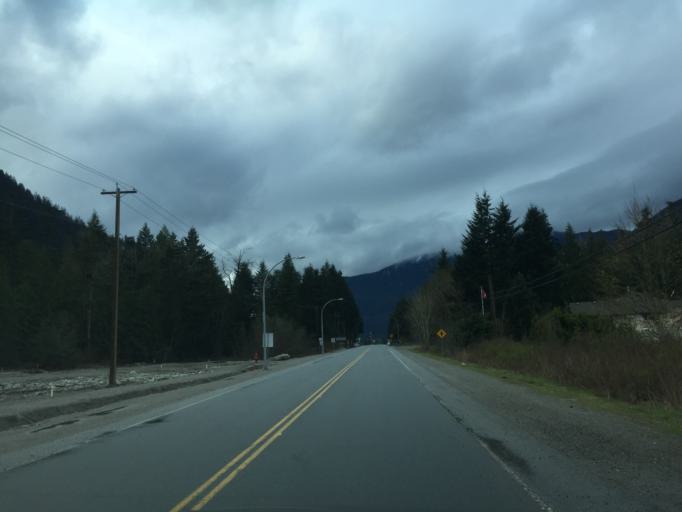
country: CA
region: British Columbia
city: Hope
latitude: 49.3617
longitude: -121.4687
